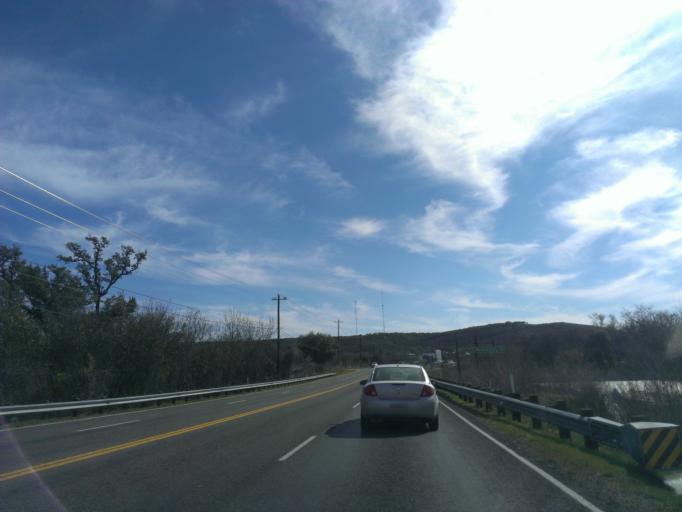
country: US
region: Texas
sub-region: Llano County
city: Kingsland
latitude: 30.6564
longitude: -98.4250
